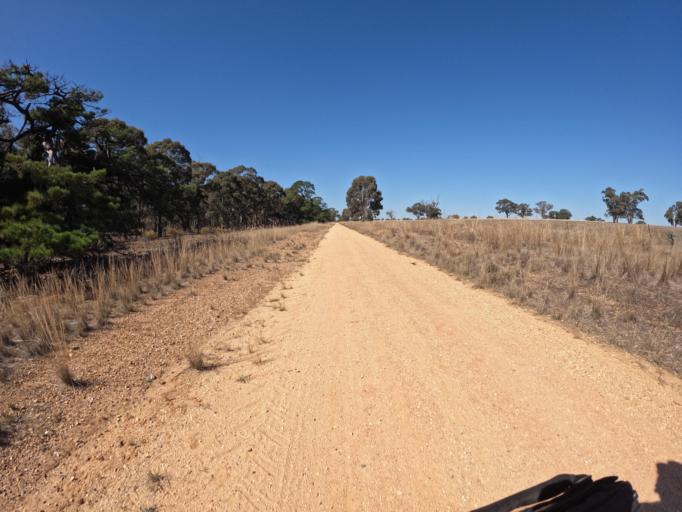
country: AU
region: Victoria
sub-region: Greater Bendigo
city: Kennington
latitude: -36.8350
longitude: 144.5963
